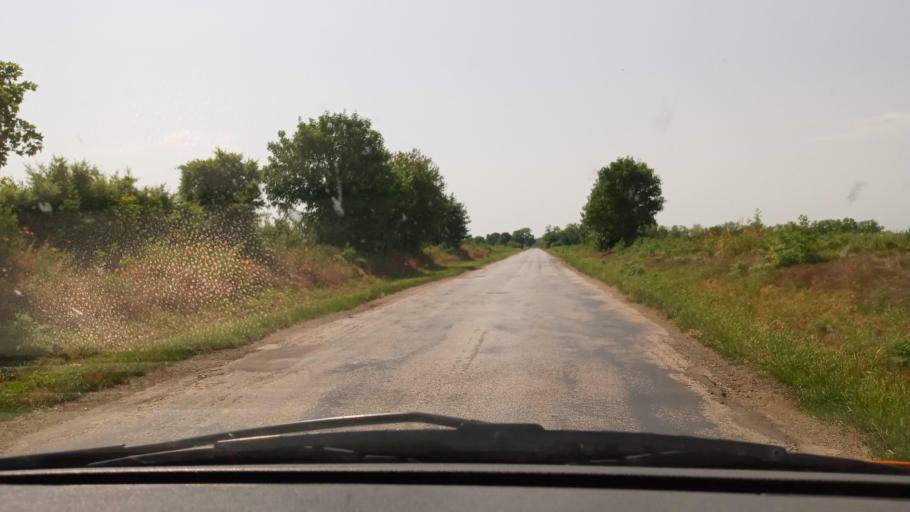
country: HU
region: Baranya
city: Szentlorinc
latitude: 46.0231
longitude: 18.0320
